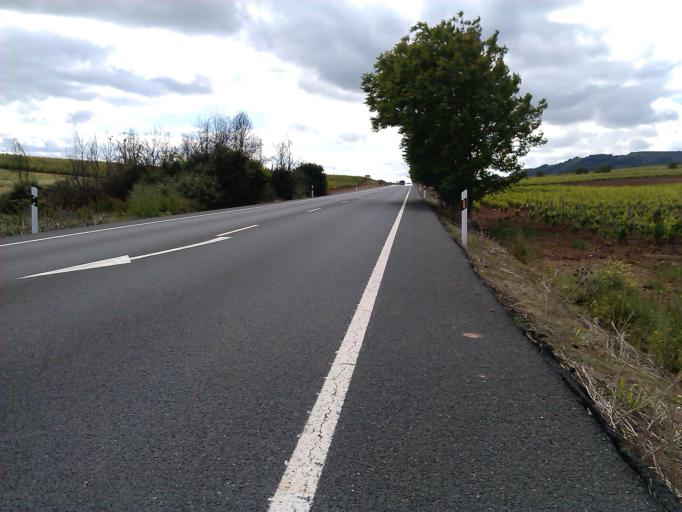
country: ES
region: La Rioja
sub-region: Provincia de La Rioja
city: Azofra
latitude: 42.4331
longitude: -2.7895
